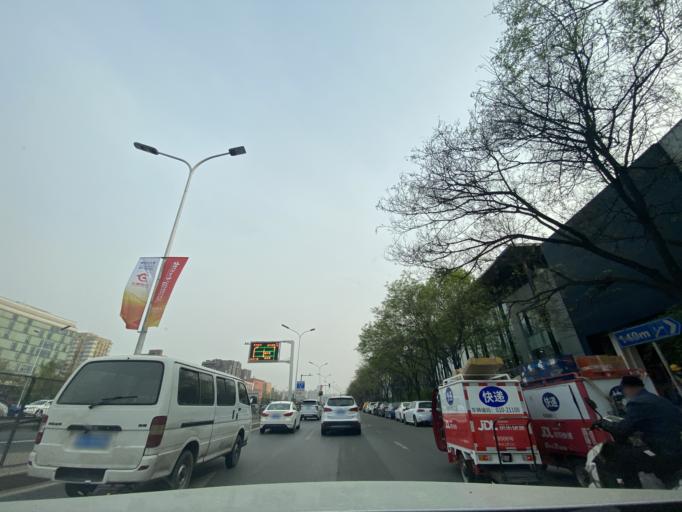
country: CN
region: Beijing
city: Sijiqing
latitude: 39.9306
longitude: 116.2686
